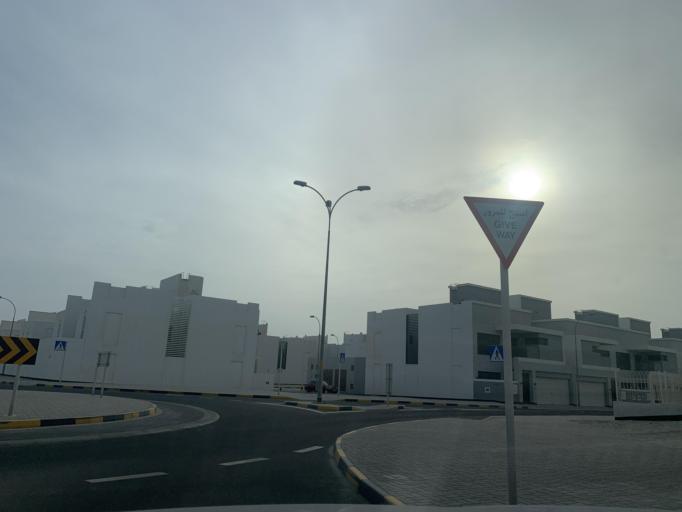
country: BH
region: Muharraq
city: Al Muharraq
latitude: 26.3148
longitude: 50.6221
